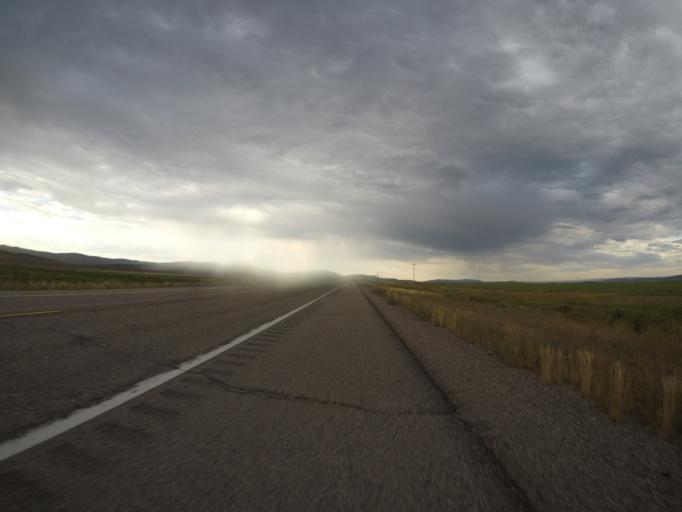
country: US
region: Utah
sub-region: Rich County
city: Randolph
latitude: 41.9213
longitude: -110.9549
